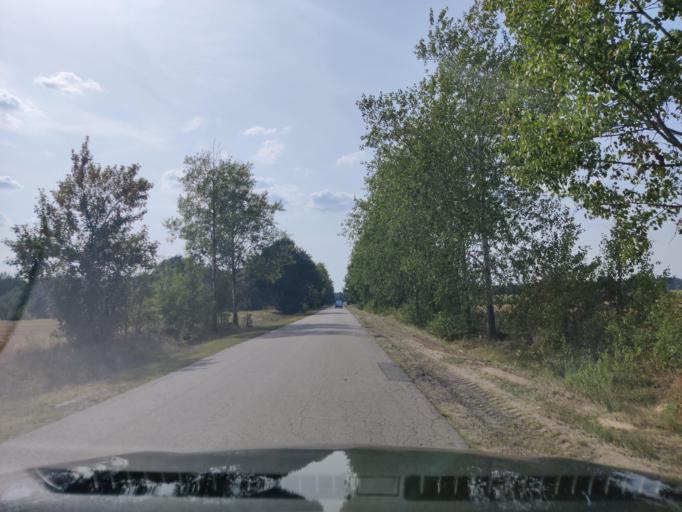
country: PL
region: Masovian Voivodeship
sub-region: Powiat wyszkowski
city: Dlugosiodlo
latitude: 52.7778
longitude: 21.4994
